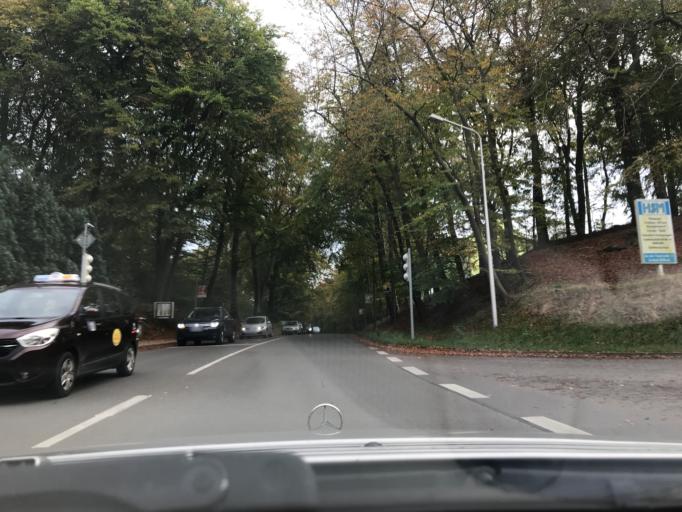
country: DE
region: Mecklenburg-Vorpommern
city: Seebad Heringsdorf
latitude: 53.9550
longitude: 14.1600
